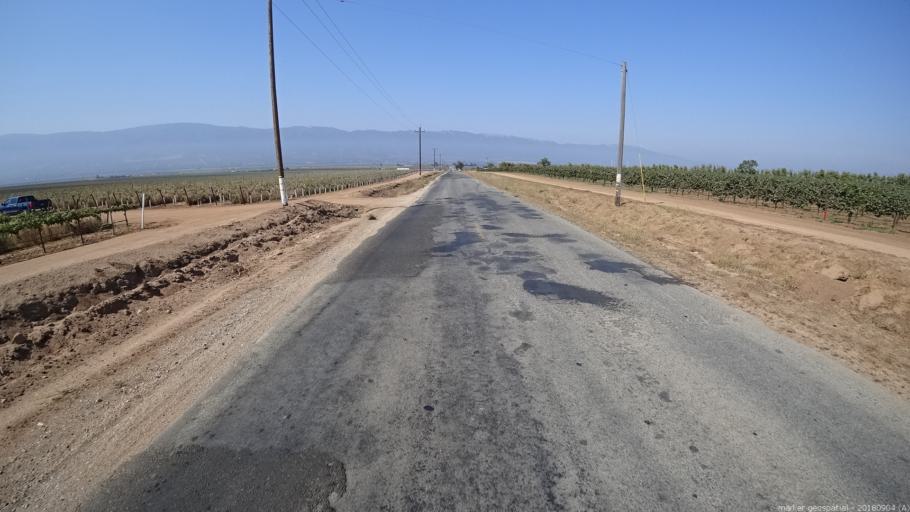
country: US
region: California
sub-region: Monterey County
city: Gonzales
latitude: 36.4984
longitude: -121.4089
